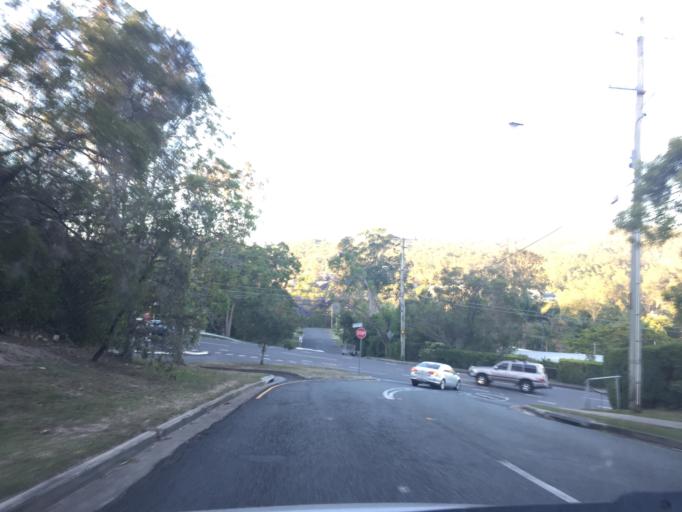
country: AU
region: Queensland
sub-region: Brisbane
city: Taringa
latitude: -27.4499
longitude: 152.9466
